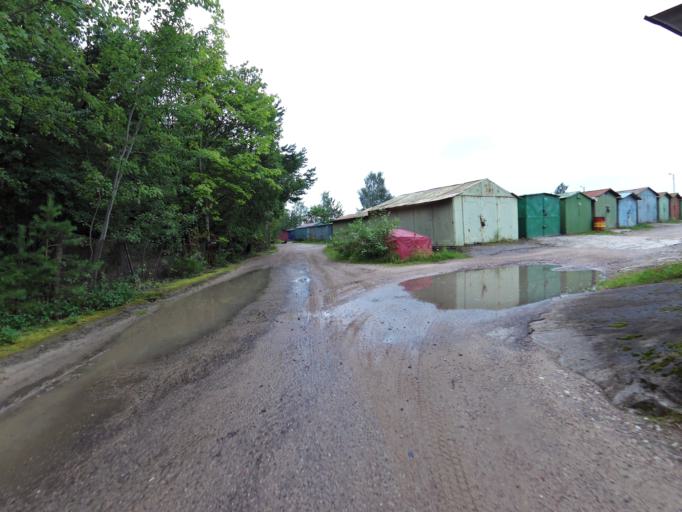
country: LT
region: Vilnius County
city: Pilaite
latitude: 54.7001
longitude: 25.2007
